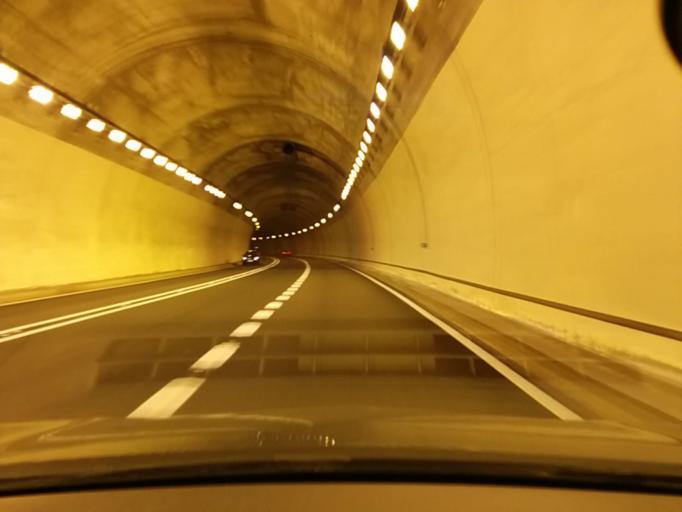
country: ES
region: Aragon
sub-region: Provincia de Huesca
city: Arguis
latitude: 42.3363
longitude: -0.3981
